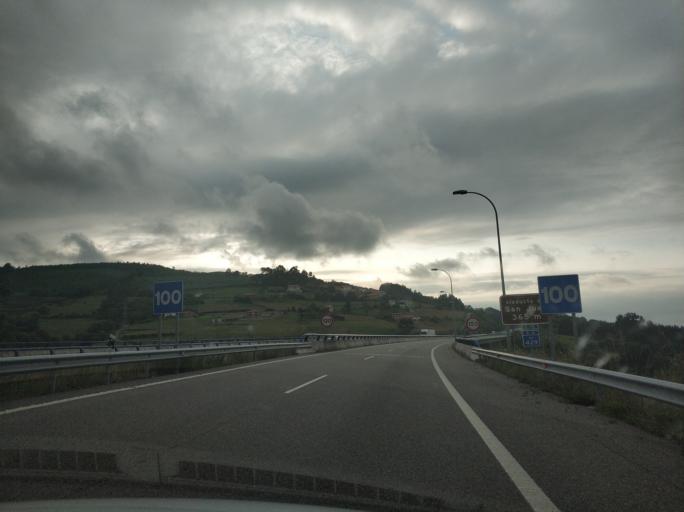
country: ES
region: Asturias
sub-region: Province of Asturias
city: Cudillero
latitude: 43.5438
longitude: -6.1557
